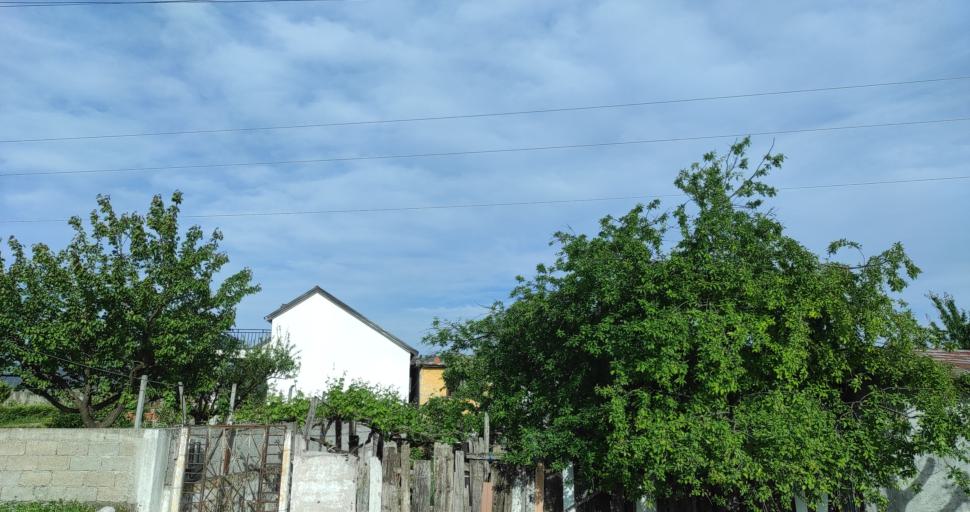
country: AL
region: Shkoder
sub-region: Rrethi i Shkodres
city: Shkoder
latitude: 42.0700
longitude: 19.5290
